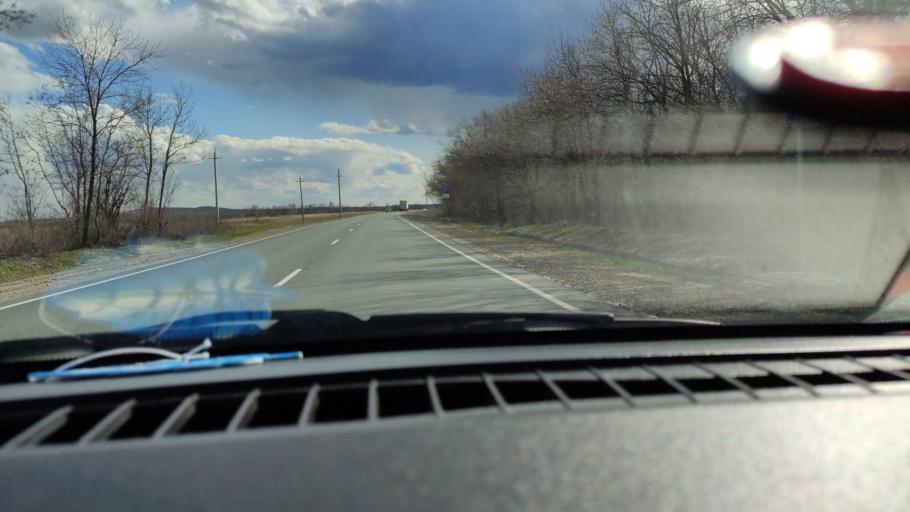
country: RU
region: Saratov
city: Alekseyevka
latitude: 52.2678
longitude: 47.9265
